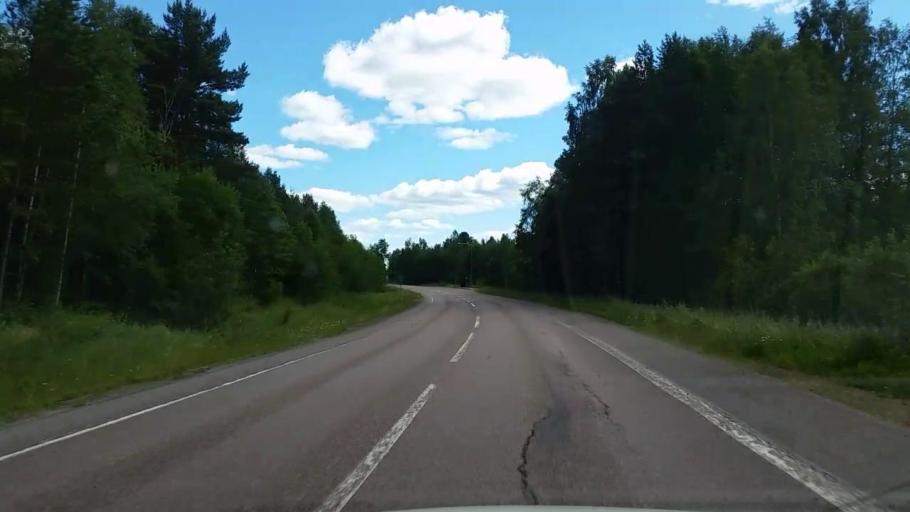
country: SE
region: Dalarna
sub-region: Faluns Kommun
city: Svardsjo
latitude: 60.8507
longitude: 15.7529
